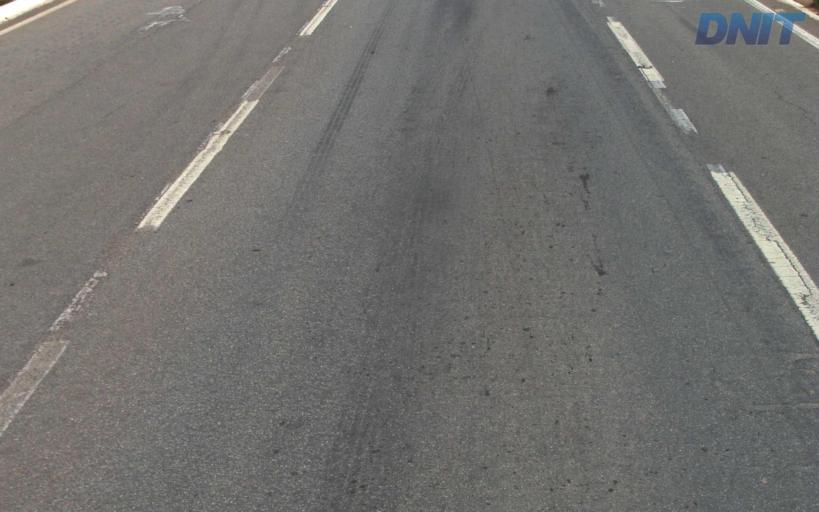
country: BR
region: Minas Gerais
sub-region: Governador Valadares
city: Governador Valadares
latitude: -18.8909
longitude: -42.0046
